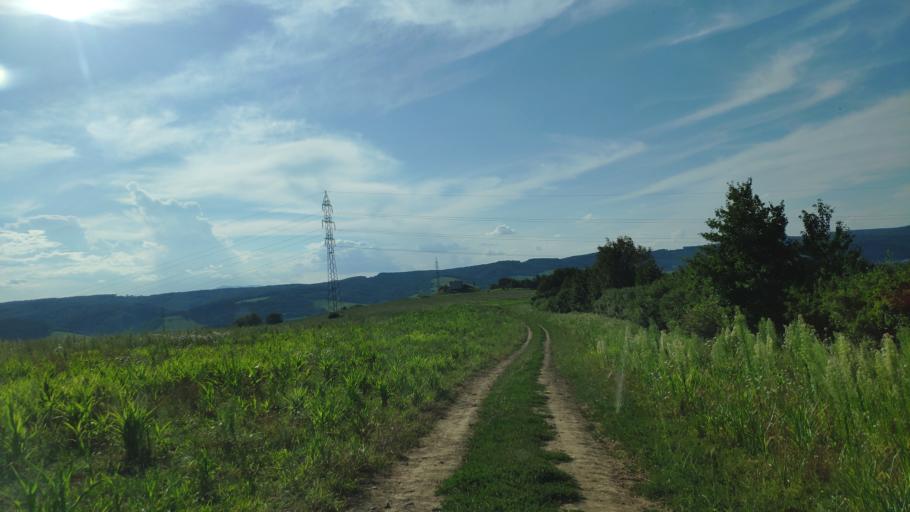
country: SK
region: Presovsky
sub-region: Okres Presov
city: Presov
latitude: 48.9137
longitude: 21.2717
